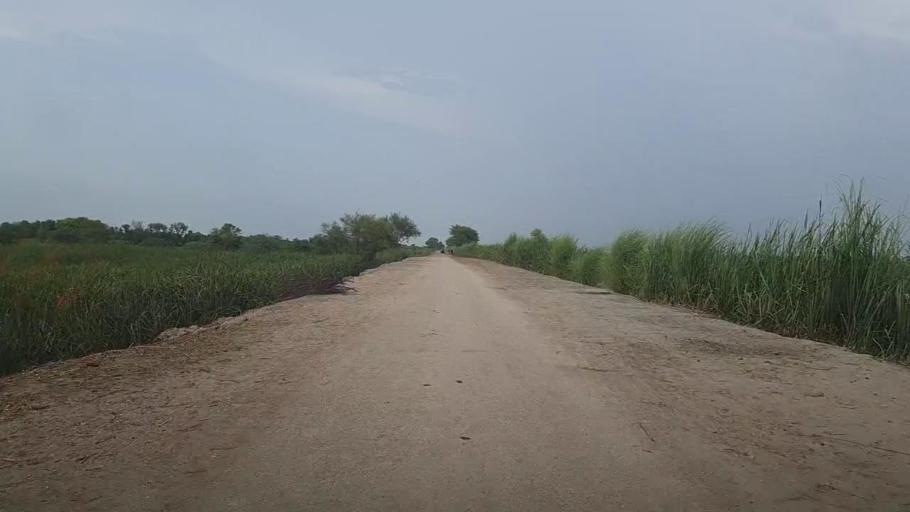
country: PK
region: Sindh
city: Karaundi
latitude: 26.9652
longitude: 68.4272
